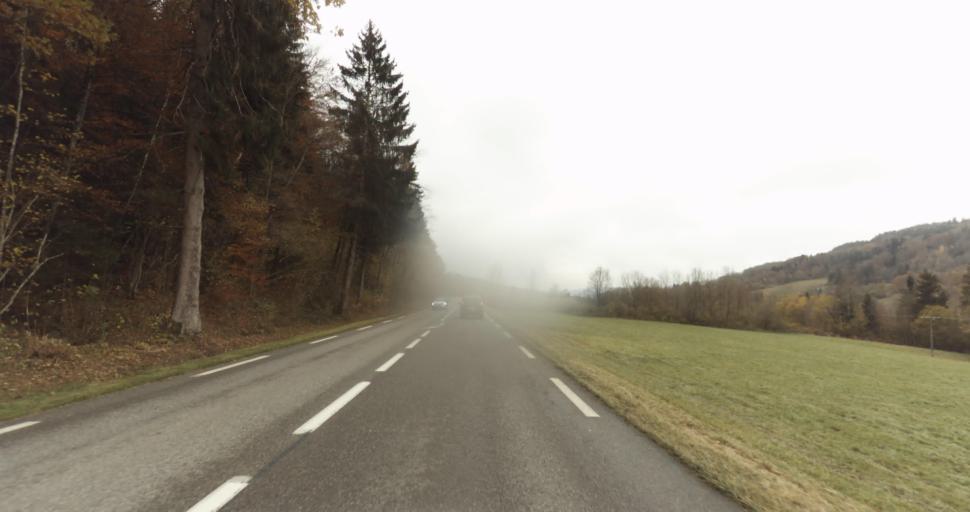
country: FR
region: Rhone-Alpes
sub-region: Departement de la Haute-Savoie
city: Evires
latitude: 46.0319
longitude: 6.2405
